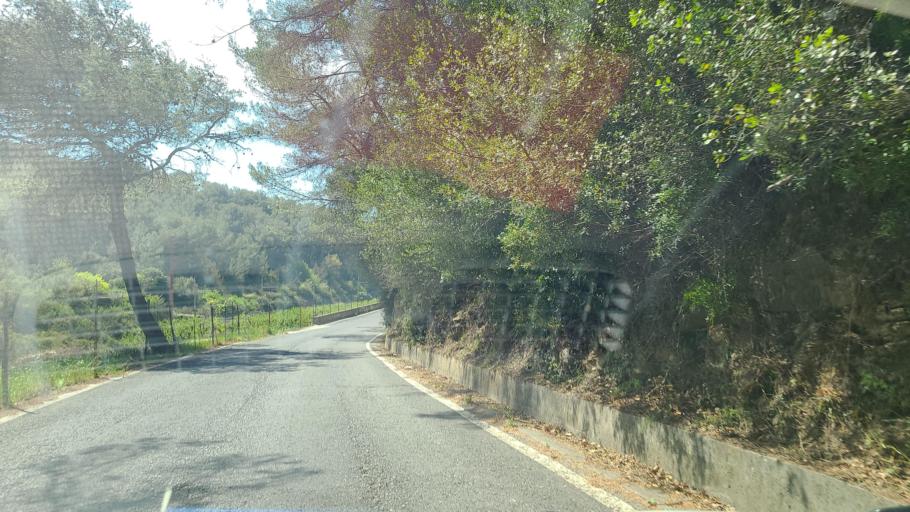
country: IT
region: Liguria
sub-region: Provincia di Savona
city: Andora
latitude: 43.9652
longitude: 8.1467
